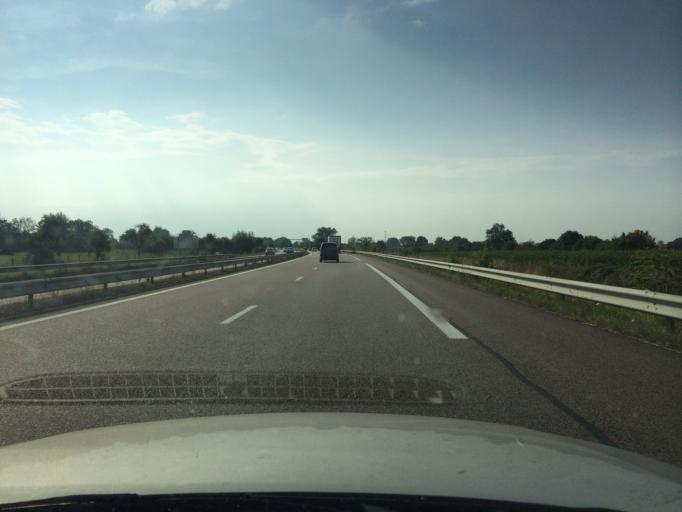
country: FR
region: Haute-Normandie
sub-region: Departement de l'Eure
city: Beuzeville
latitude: 49.3359
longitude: 0.3826
